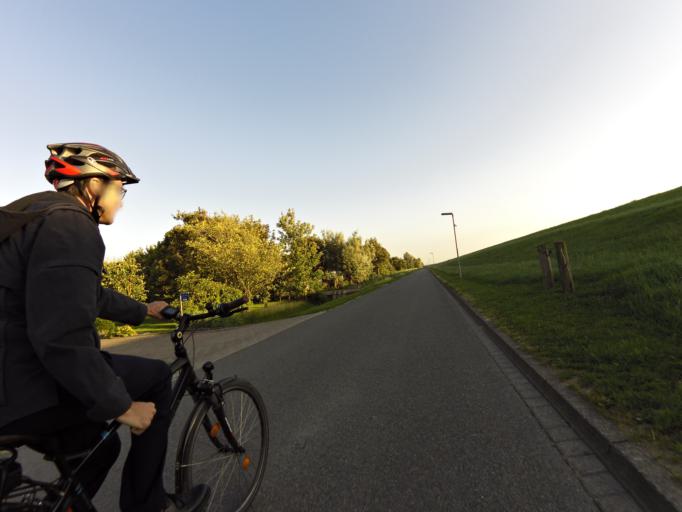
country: DE
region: Lower Saxony
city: Cappel
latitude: 53.7610
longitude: 8.5366
